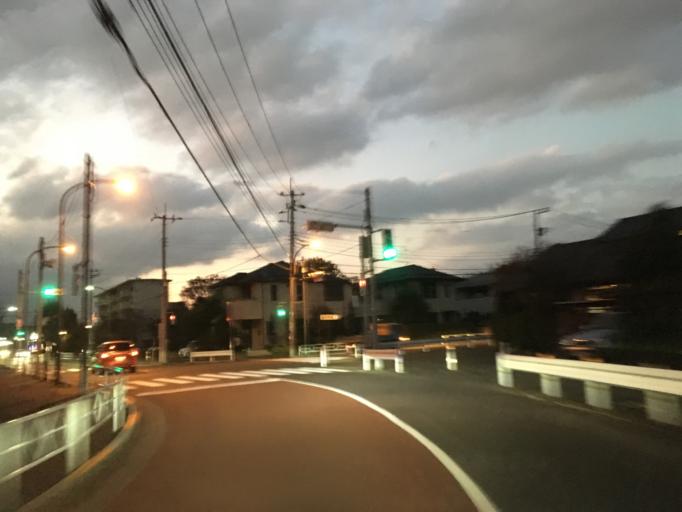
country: JP
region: Tokyo
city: Kokubunji
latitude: 35.7183
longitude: 139.4393
